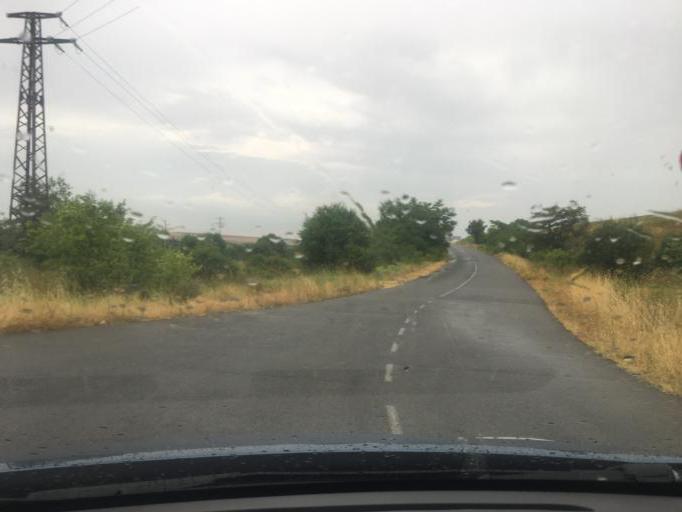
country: BG
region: Burgas
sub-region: Obshtina Burgas
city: Burgas
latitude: 42.5508
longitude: 27.4899
